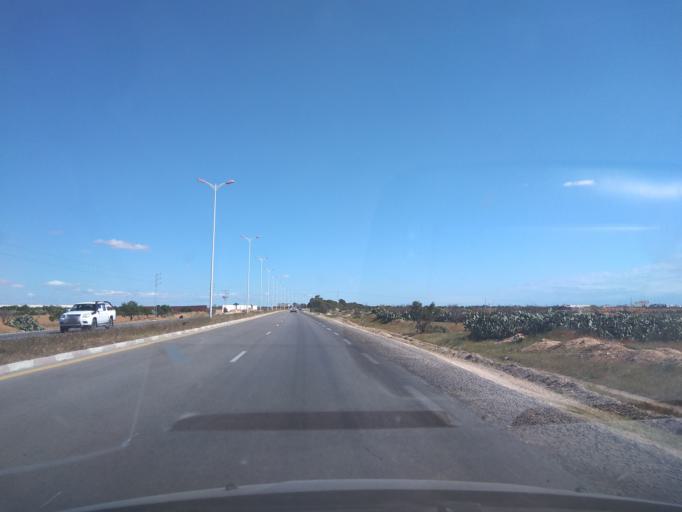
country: TN
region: Safaqis
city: Al Qarmadah
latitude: 34.8388
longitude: 10.7360
